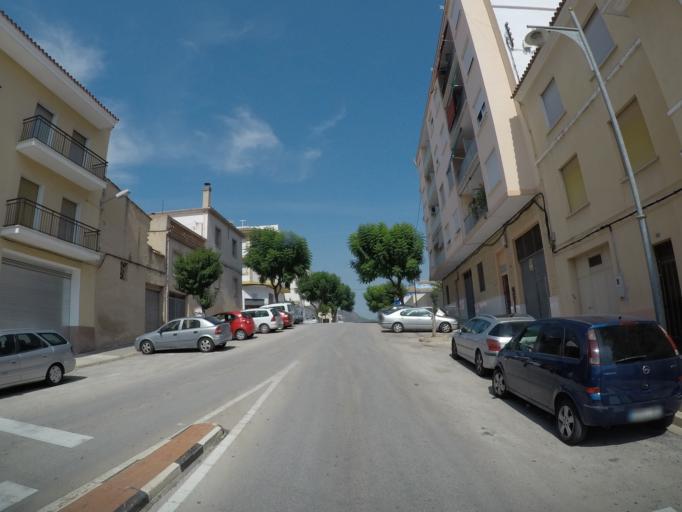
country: ES
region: Valencia
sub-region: Provincia de Alicante
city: Pego
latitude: 38.8412
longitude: -0.1129
